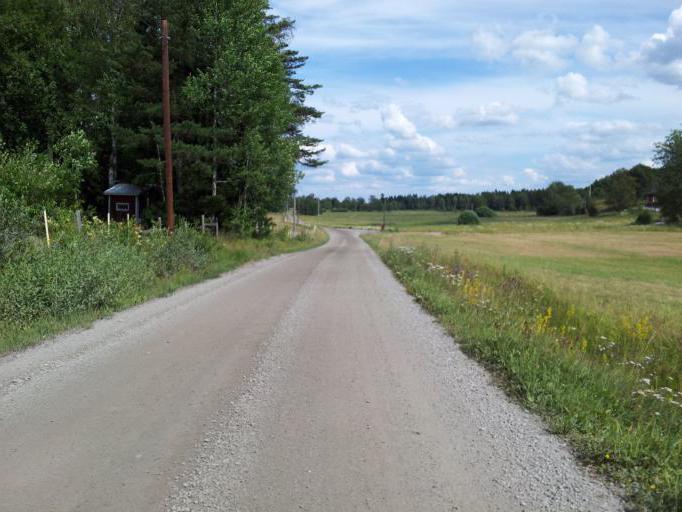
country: SE
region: Stockholm
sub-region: Norrtalje Kommun
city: Nykvarn
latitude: 59.8500
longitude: 18.2563
